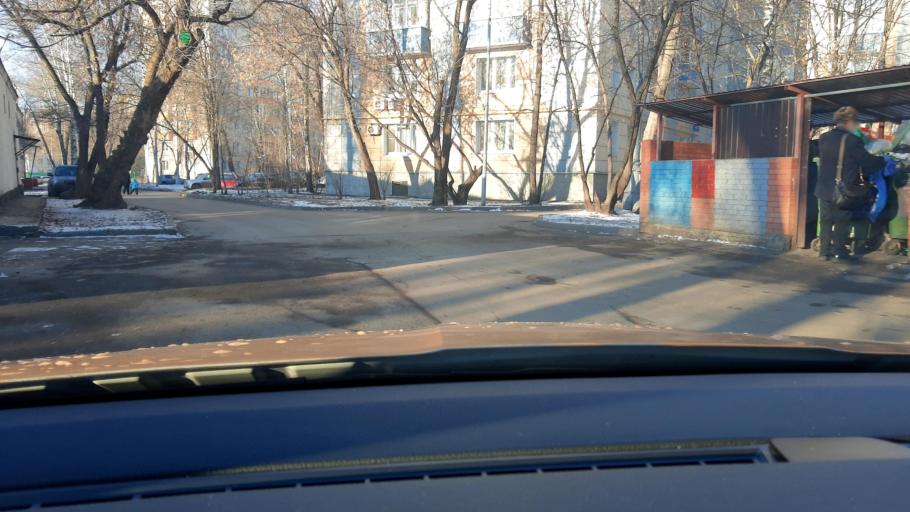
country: RU
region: Moscow
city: Novokuz'minki
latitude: 55.7062
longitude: 37.7873
